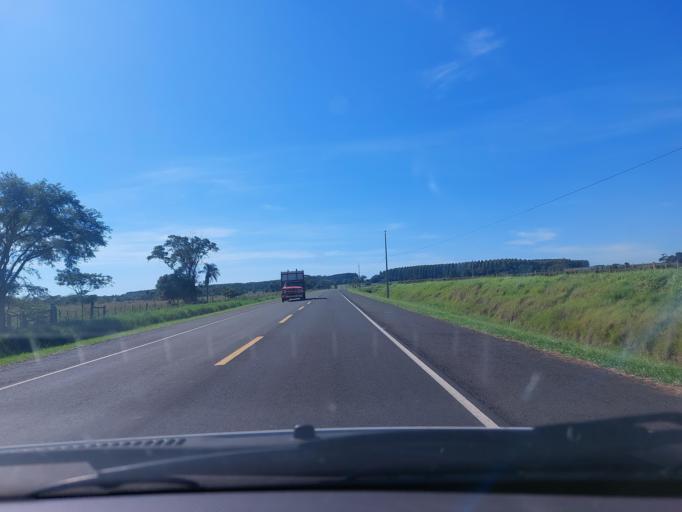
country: PY
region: San Pedro
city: Itacurubi del Rosario
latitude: -24.6037
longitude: -56.7739
